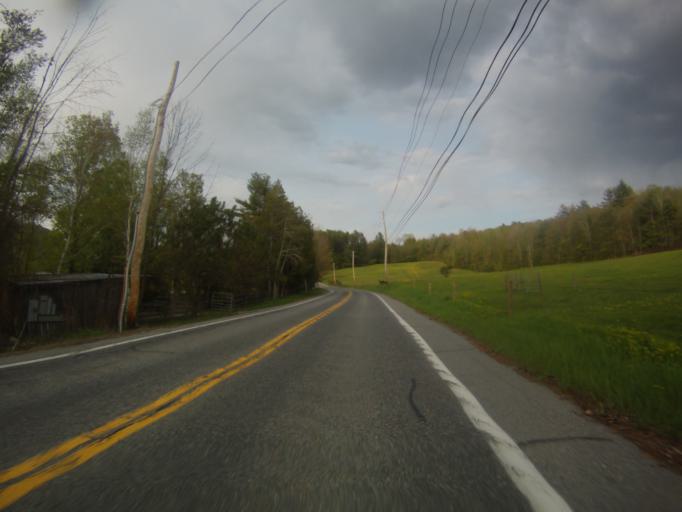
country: US
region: New York
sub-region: Warren County
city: Warrensburg
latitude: 43.7076
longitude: -73.7065
